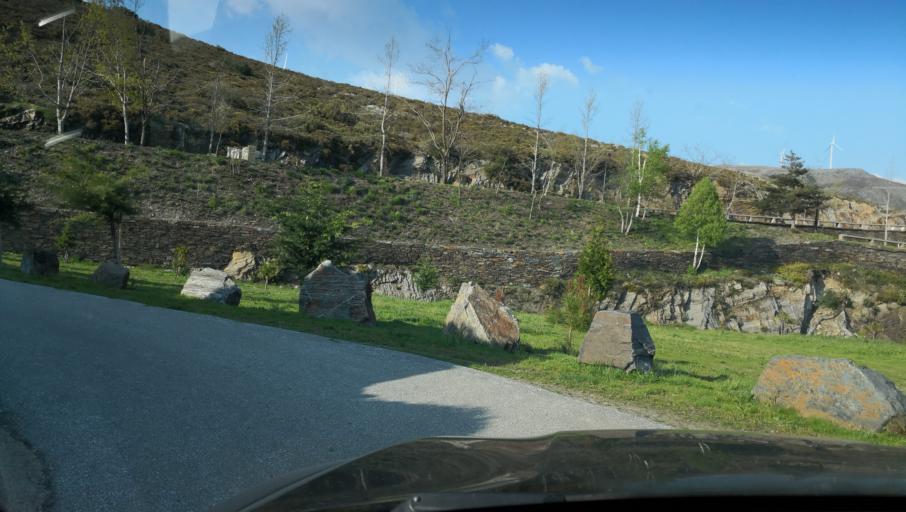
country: PT
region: Vila Real
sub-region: Vila Real
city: Vila Real
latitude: 41.3188
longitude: -7.8599
